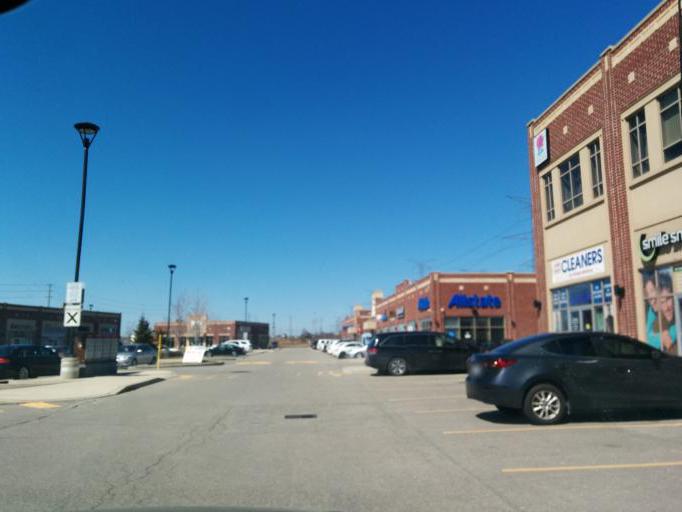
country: CA
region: Ontario
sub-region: Halton
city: Milton
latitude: 43.5393
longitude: -79.8566
